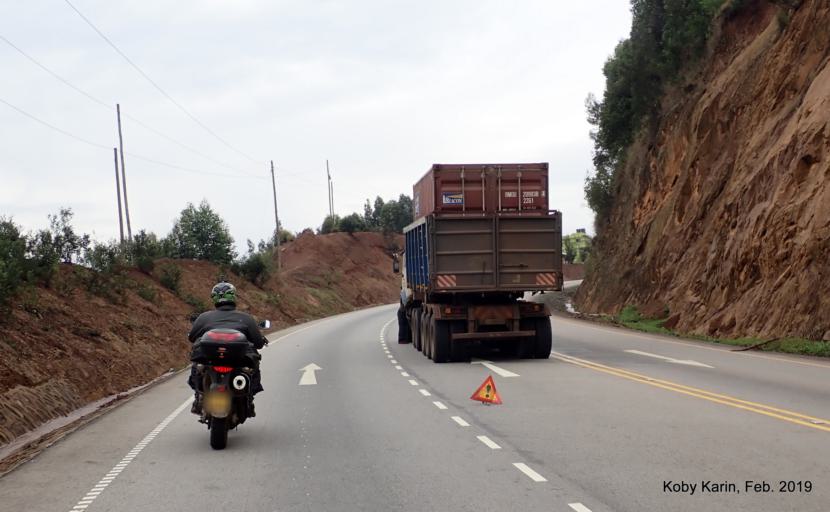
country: UG
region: Western Region
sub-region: Kabale District
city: Kabale
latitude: -1.2367
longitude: 30.0544
